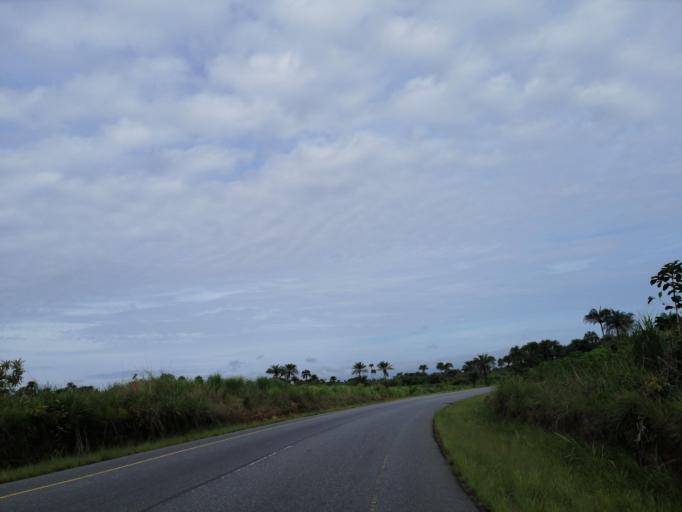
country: SL
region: Northern Province
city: Port Loko
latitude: 8.7724
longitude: -12.8600
